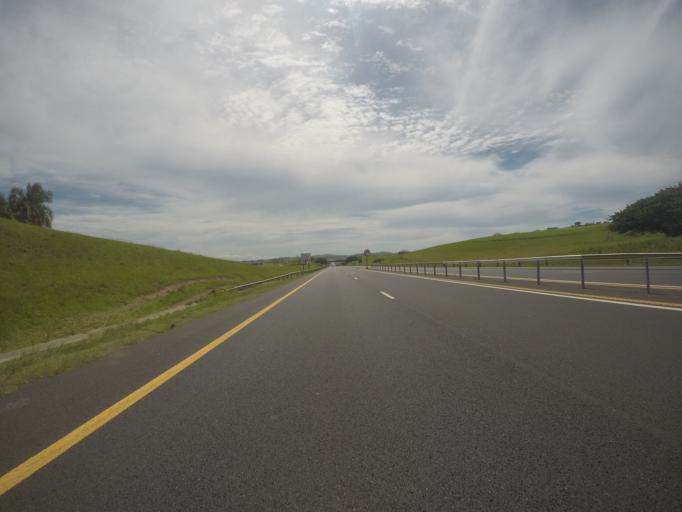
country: ZA
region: KwaZulu-Natal
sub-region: iLembe District Municipality
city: Mandeni
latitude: -29.1748
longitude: 31.5109
